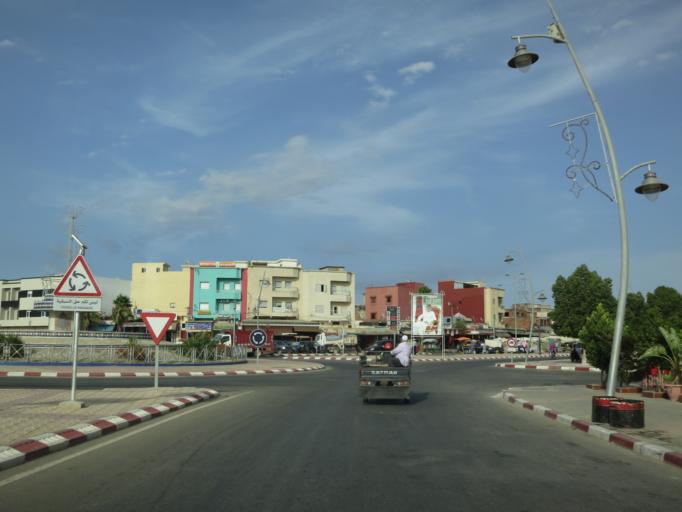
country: MA
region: Gharb-Chrarda-Beni Hssen
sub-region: Sidi-Kacem
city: Sidi Bousber
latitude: 34.4896
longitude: -5.5143
